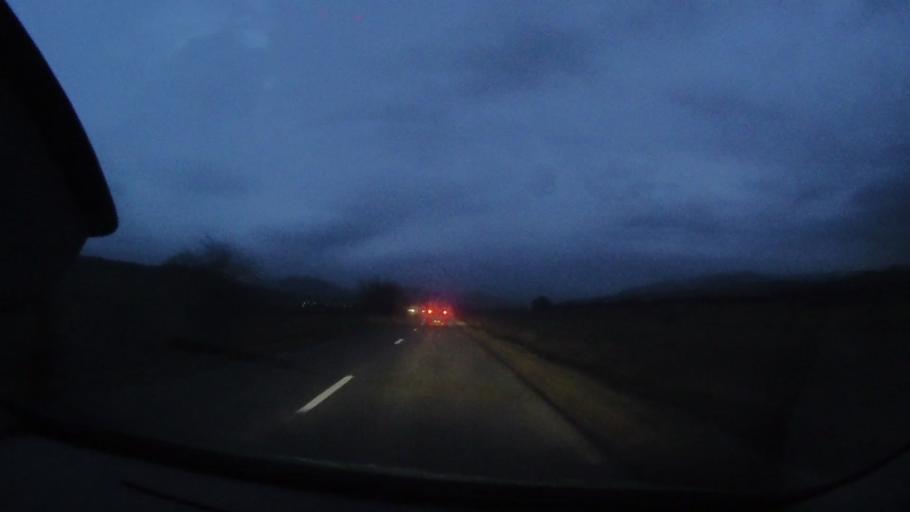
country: RO
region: Mures
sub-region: Comuna Hodac
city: Hodac
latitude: 46.7726
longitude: 24.8966
